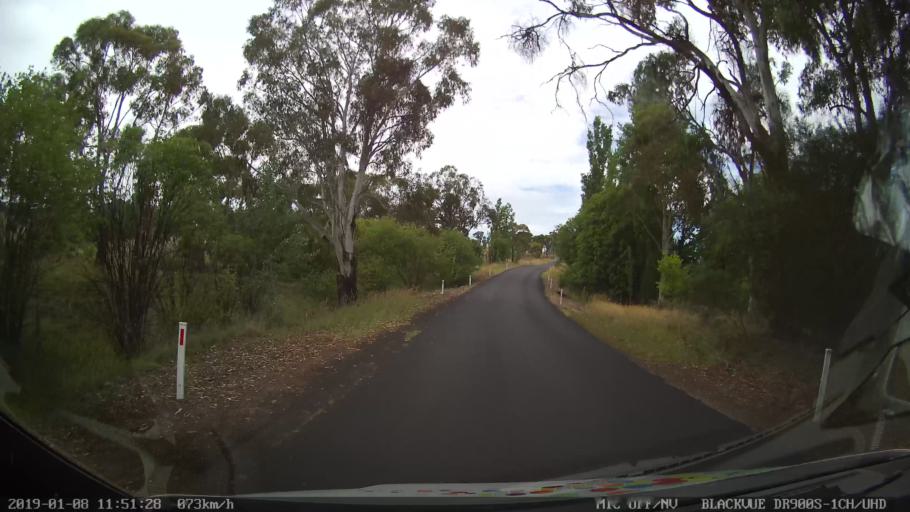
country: AU
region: New South Wales
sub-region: Armidale Dumaresq
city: Armidale
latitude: -30.3932
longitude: 151.5601
